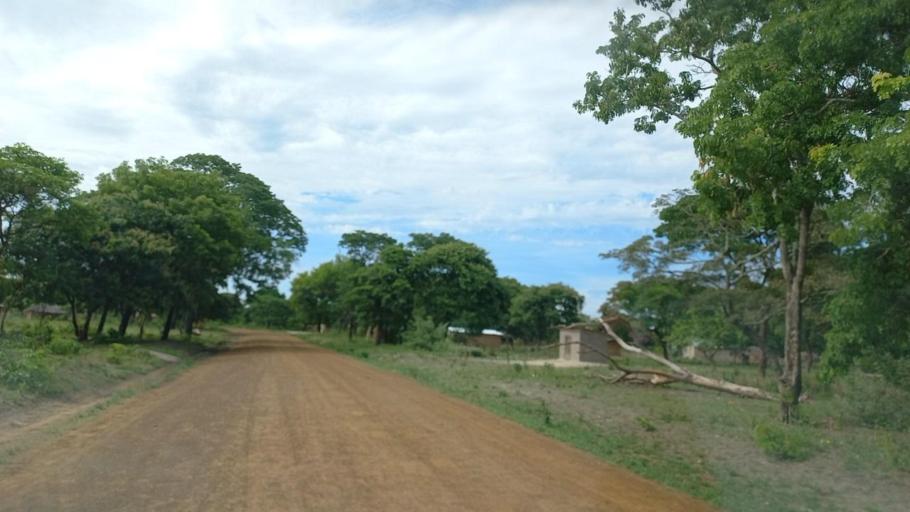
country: ZM
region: North-Western
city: Kabompo
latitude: -13.4594
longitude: 24.4271
